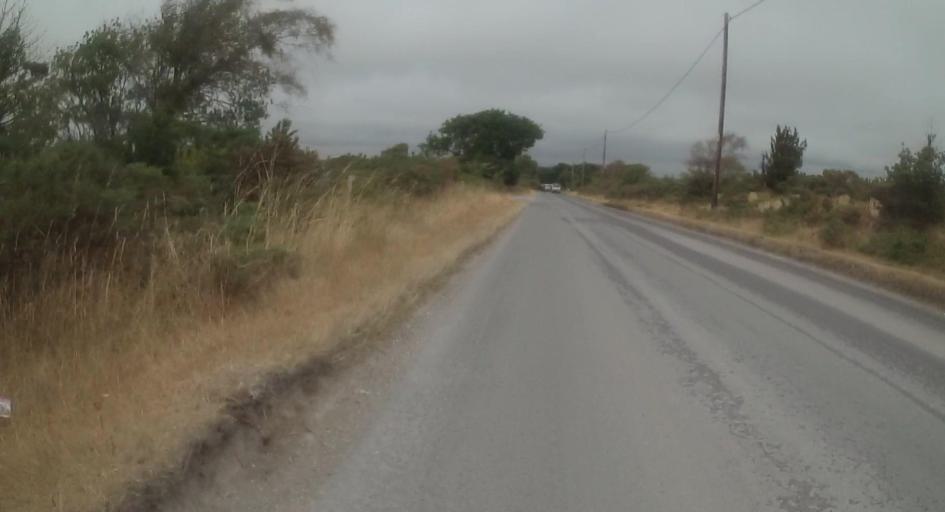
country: GB
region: England
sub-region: Dorset
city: Wareham
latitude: 50.6608
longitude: -2.1007
